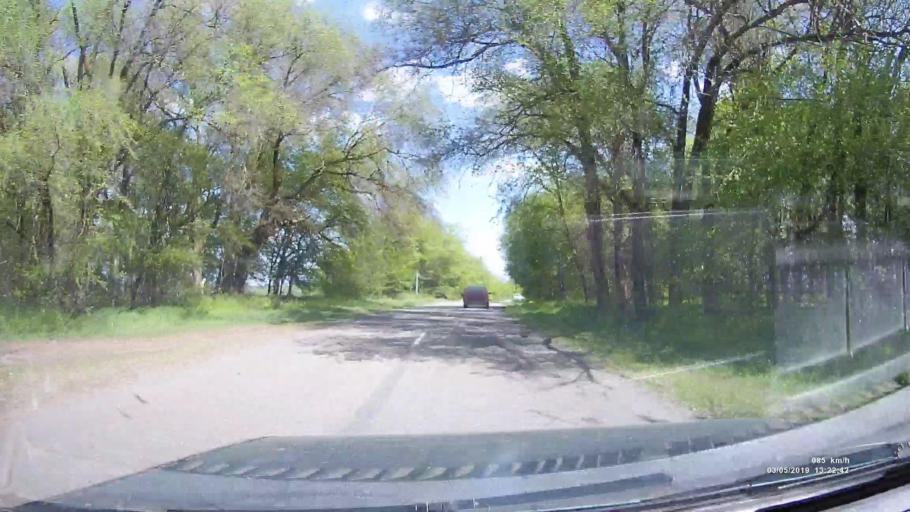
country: RU
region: Rostov
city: Semikarakorsk
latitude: 47.5624
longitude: 40.7664
